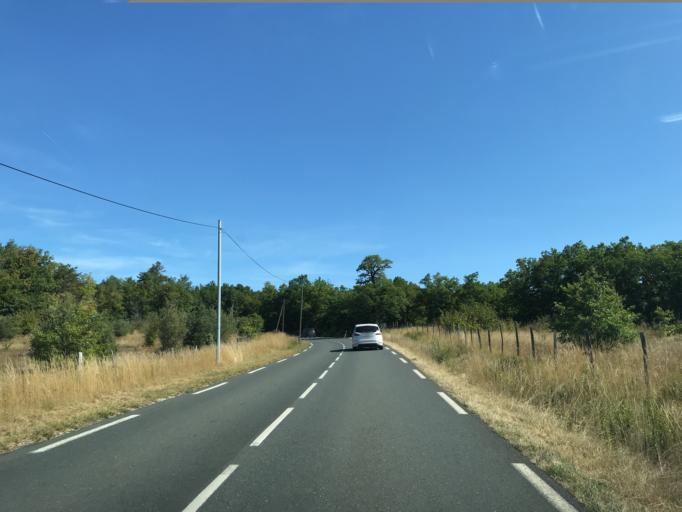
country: FR
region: Limousin
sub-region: Departement de la Correze
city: Larche
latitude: 45.0781
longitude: 1.3779
